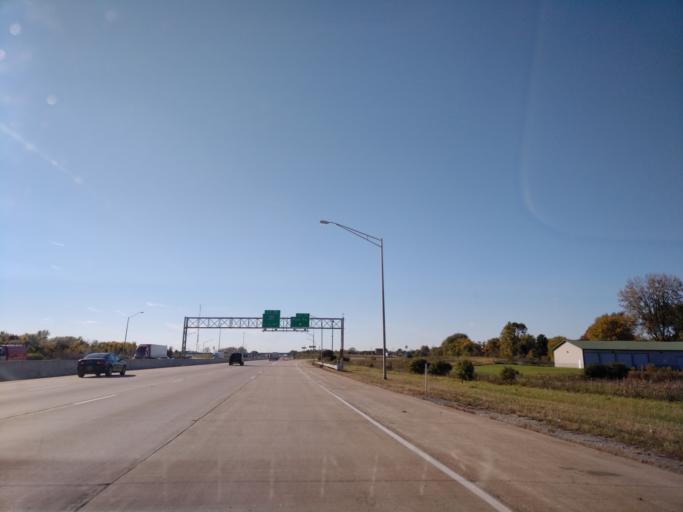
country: US
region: Indiana
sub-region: Marion County
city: Lawrence
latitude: 39.8013
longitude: -86.0019
